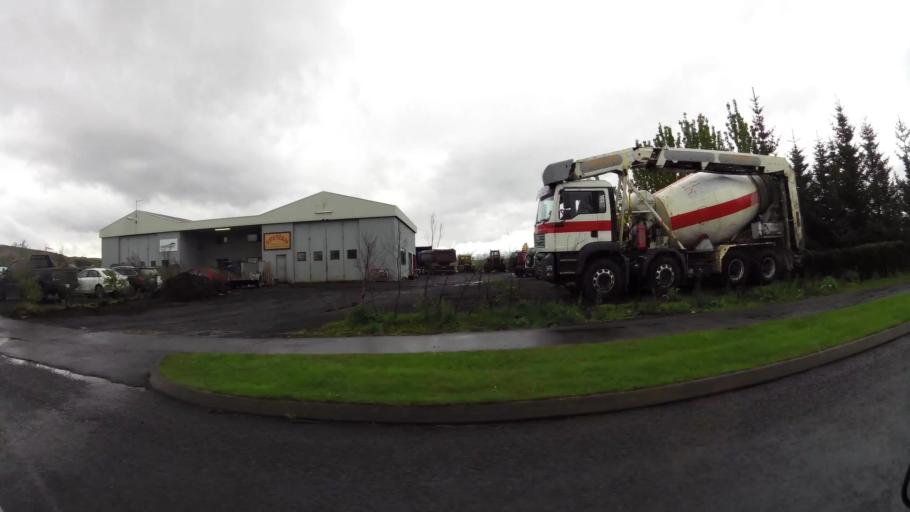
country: IS
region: South
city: Vestmannaeyjar
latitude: 63.7499
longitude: -20.2235
